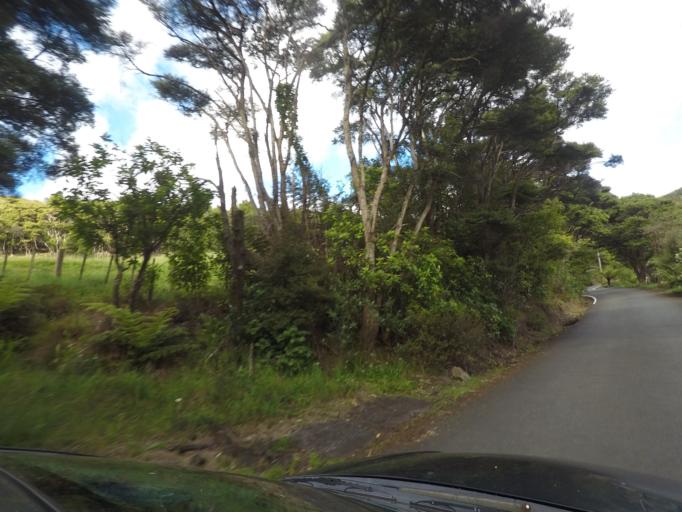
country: NZ
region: Auckland
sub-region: Auckland
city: Titirangi
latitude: -37.0199
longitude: 174.5498
